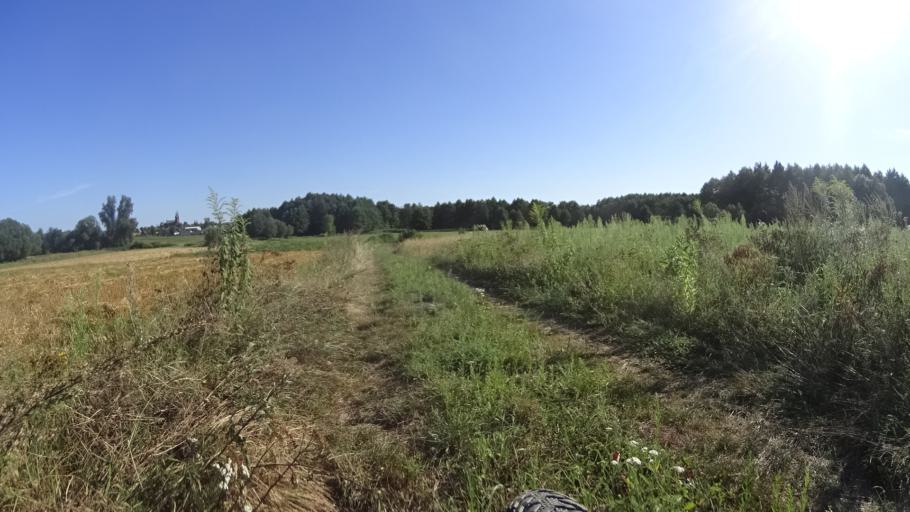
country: PL
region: Masovian Voivodeship
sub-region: Powiat bialobrzeski
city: Wysmierzyce
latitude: 51.6715
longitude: 20.8454
